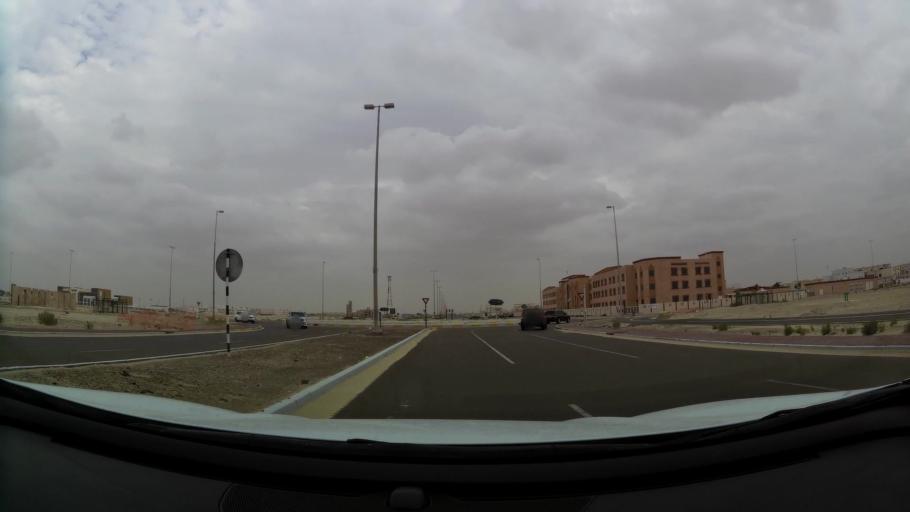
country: AE
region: Abu Dhabi
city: Abu Dhabi
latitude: 24.3628
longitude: 54.6323
